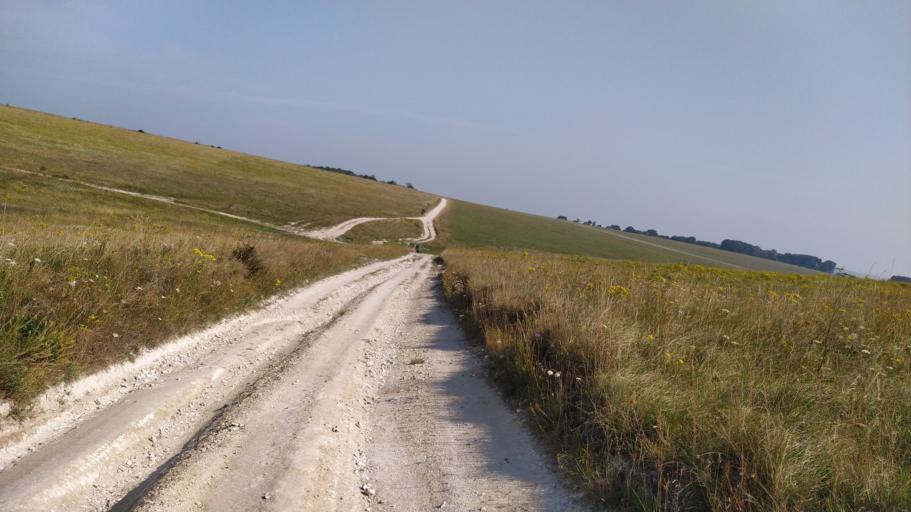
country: GB
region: England
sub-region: Wiltshire
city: Shrewton
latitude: 51.1794
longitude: -1.9517
